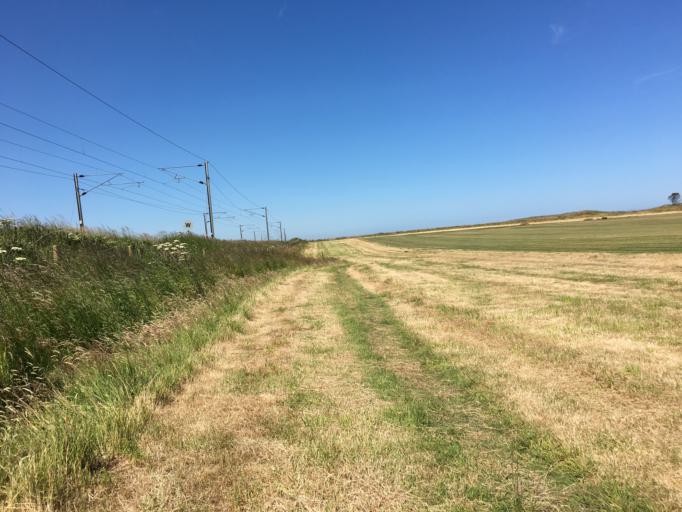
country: GB
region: England
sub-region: Northumberland
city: Ancroft
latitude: 55.7080
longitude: -1.9301
